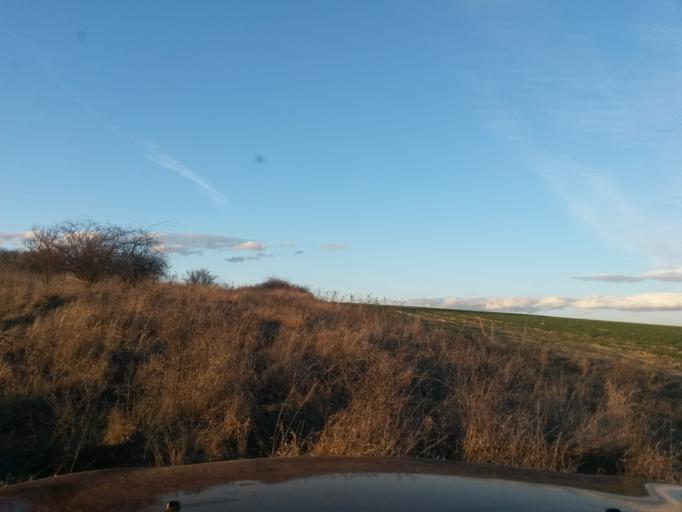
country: SK
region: Kosicky
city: Kosice
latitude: 48.7062
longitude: 21.3127
